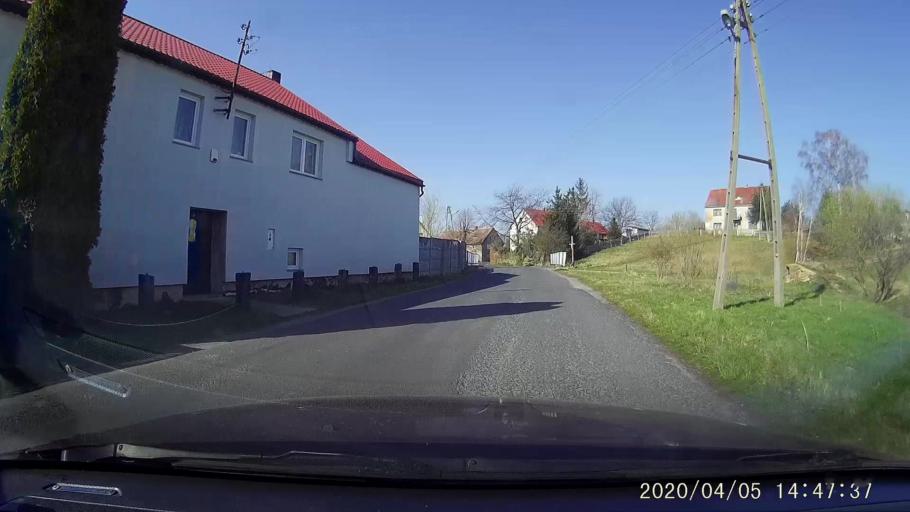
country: PL
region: Lower Silesian Voivodeship
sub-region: Powiat zgorzelecki
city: Sulikow
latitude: 51.0649
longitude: 15.1060
